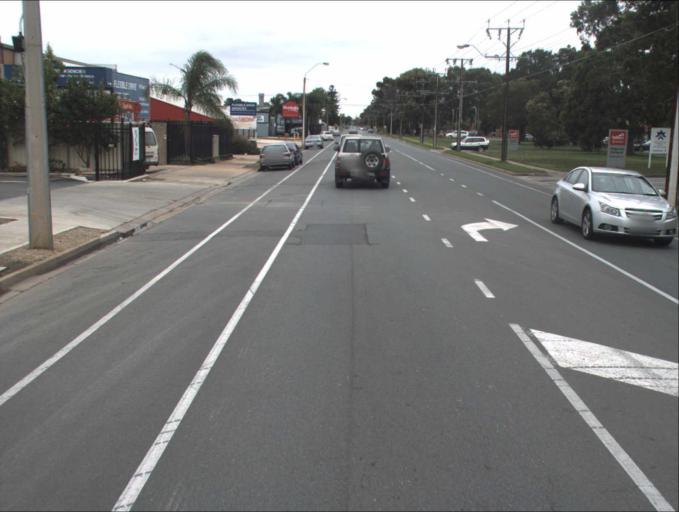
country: AU
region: South Australia
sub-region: Charles Sturt
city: Woodville
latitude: -34.8729
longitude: 138.5661
